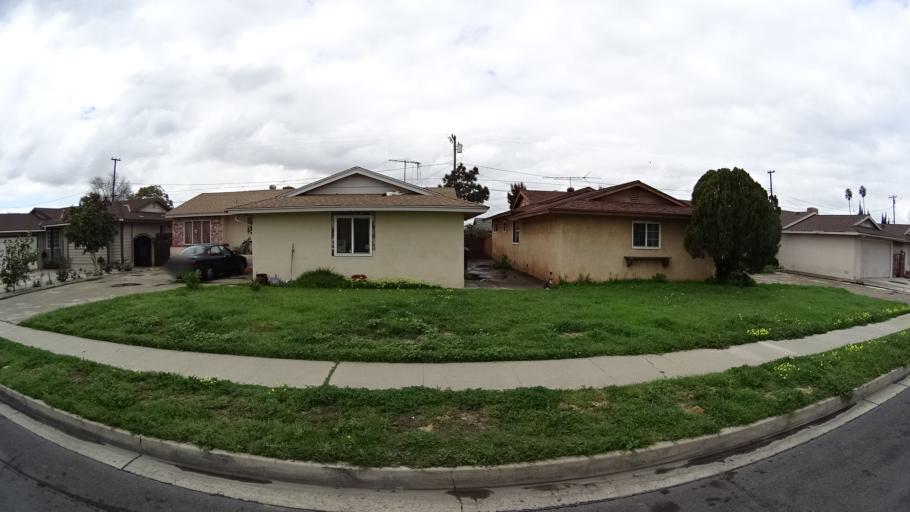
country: US
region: California
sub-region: Orange County
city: Anaheim
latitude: 33.8308
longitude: -117.9485
